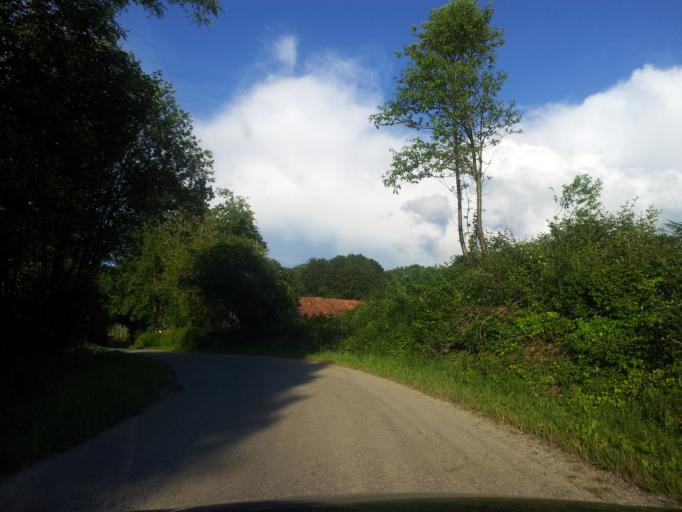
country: HR
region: Karlovacka
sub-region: Grad Karlovac
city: Karlovac
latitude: 45.4727
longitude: 15.4706
